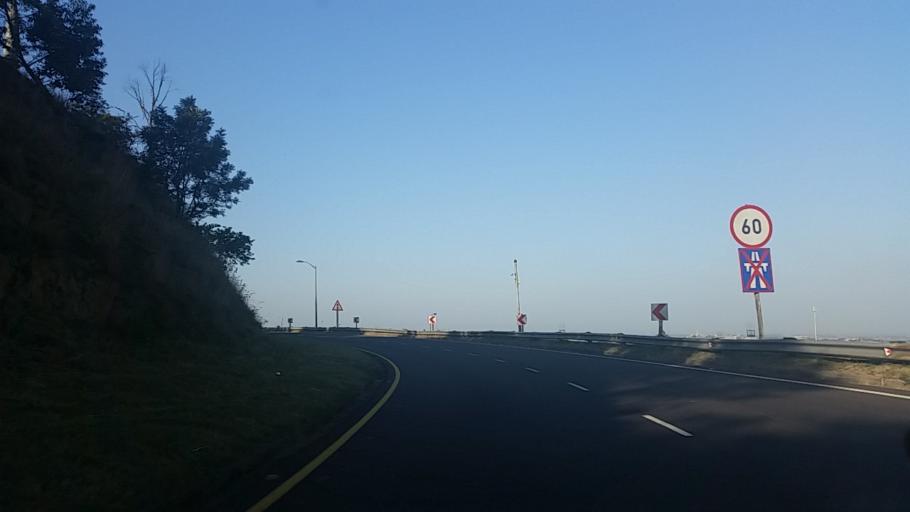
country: ZA
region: KwaZulu-Natal
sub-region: eThekwini Metropolitan Municipality
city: Berea
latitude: -29.8471
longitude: 30.9283
